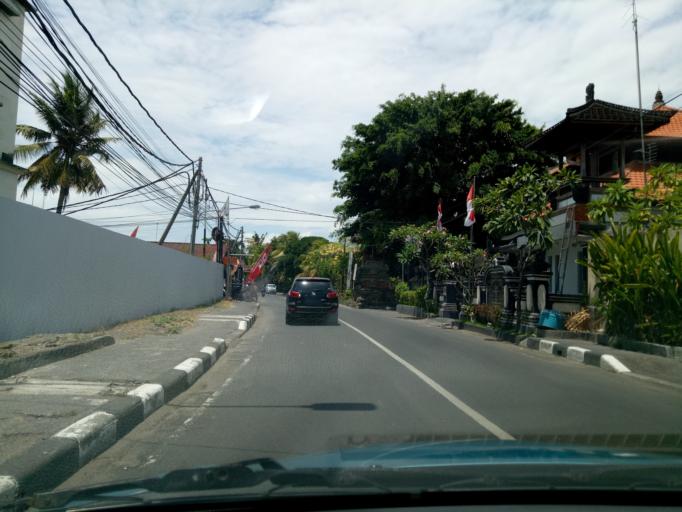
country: ID
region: Bali
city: Banjar Medura
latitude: -8.7057
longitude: 115.2537
